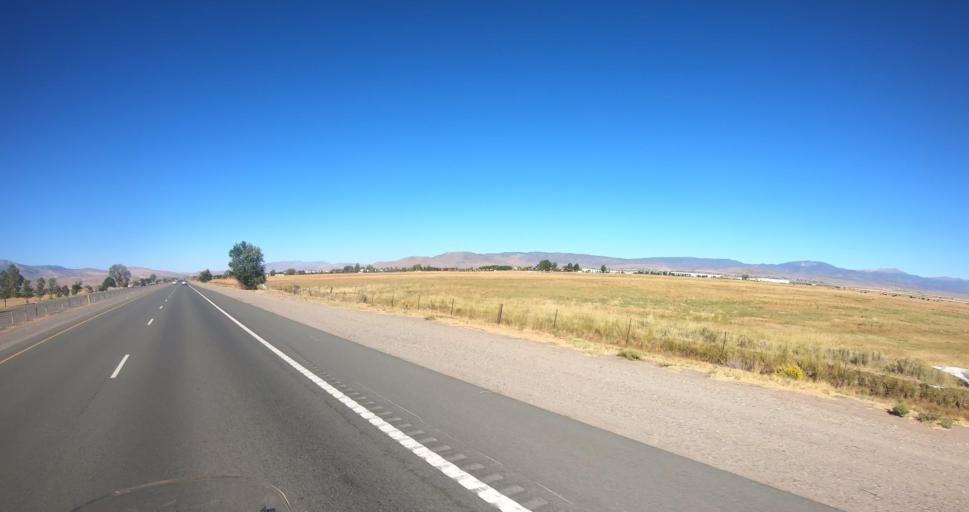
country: US
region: Nevada
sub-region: Douglas County
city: Minden
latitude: 38.9879
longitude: -119.7841
